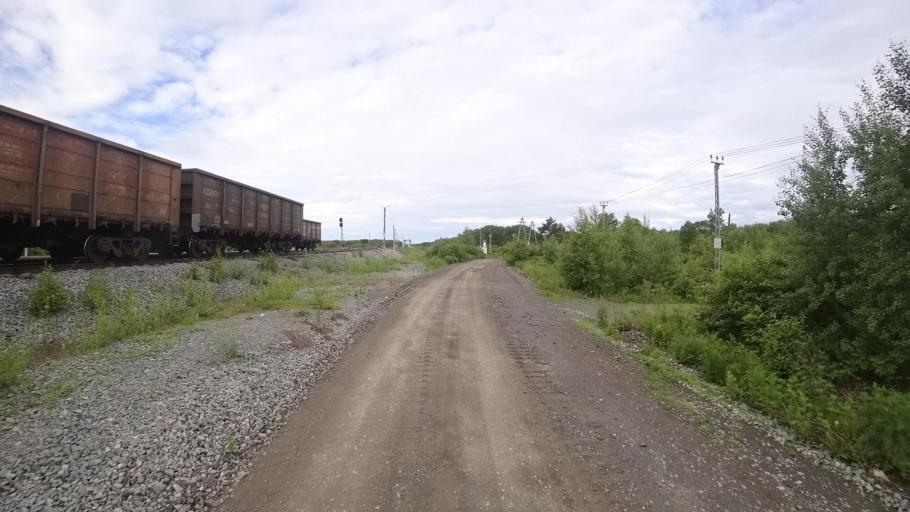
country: RU
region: Khabarovsk Krai
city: Amursk
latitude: 49.8946
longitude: 136.1278
